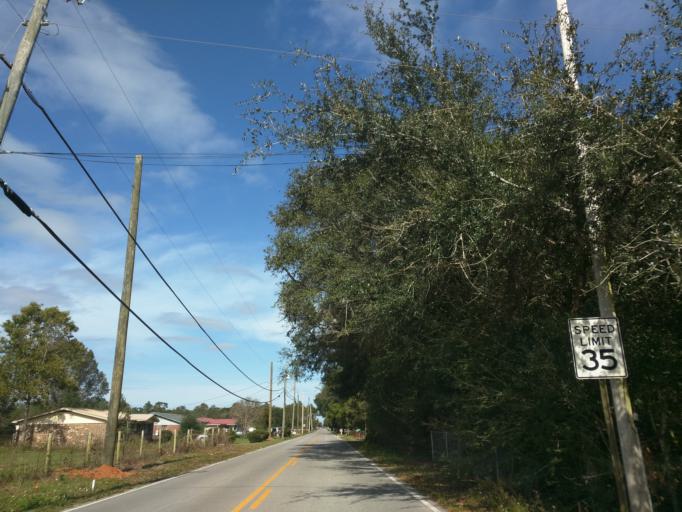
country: US
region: Florida
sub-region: Escambia County
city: Cantonment
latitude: 30.5371
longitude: -87.4060
